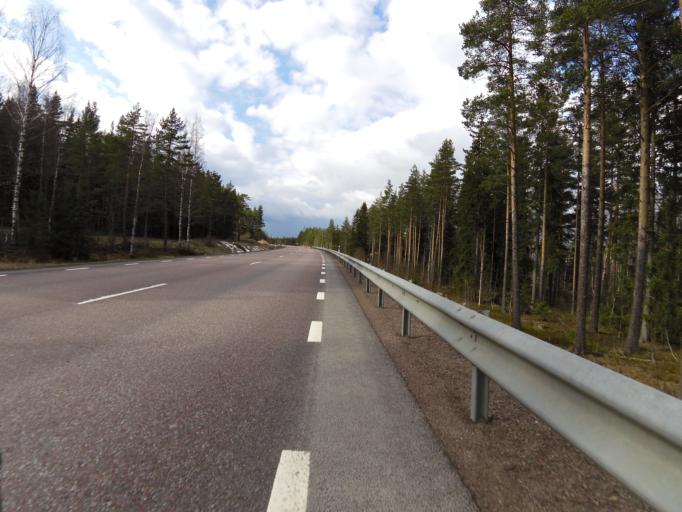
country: SE
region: Gaevleborg
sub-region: Hofors Kommun
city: Hofors
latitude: 60.4912
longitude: 16.4412
